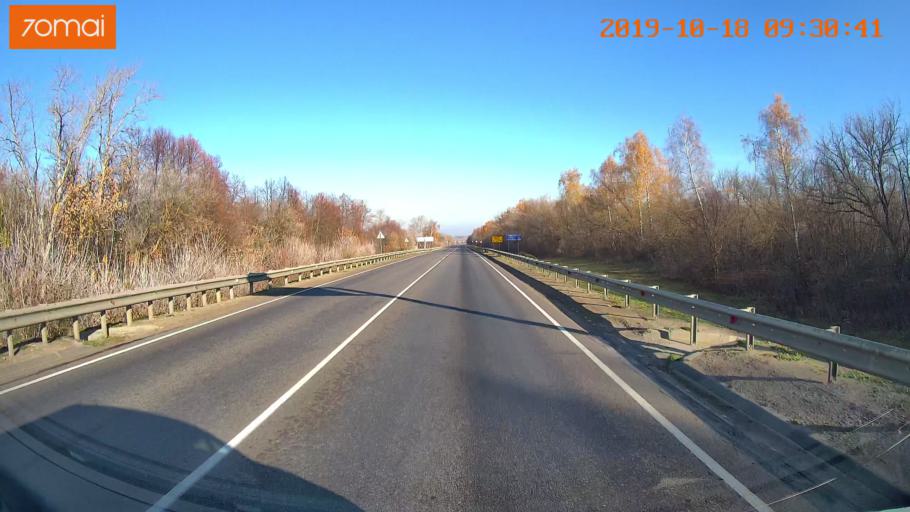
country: RU
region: Tula
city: Yefremov
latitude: 53.1410
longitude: 38.1595
